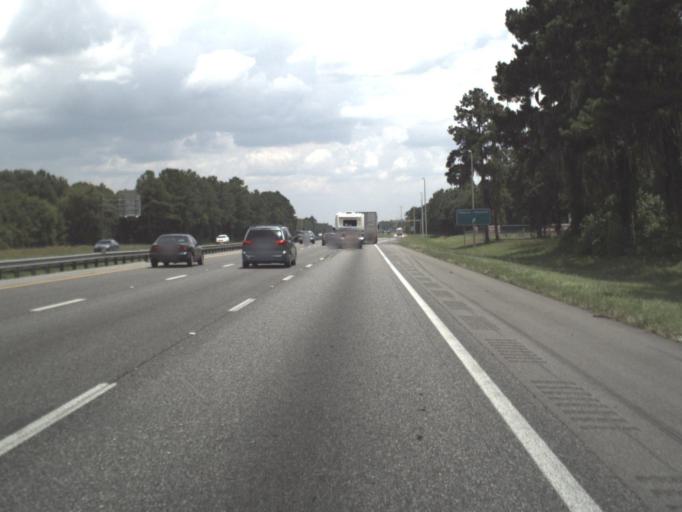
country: US
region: Florida
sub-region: Hamilton County
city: Jasper
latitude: 30.4317
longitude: -82.9107
